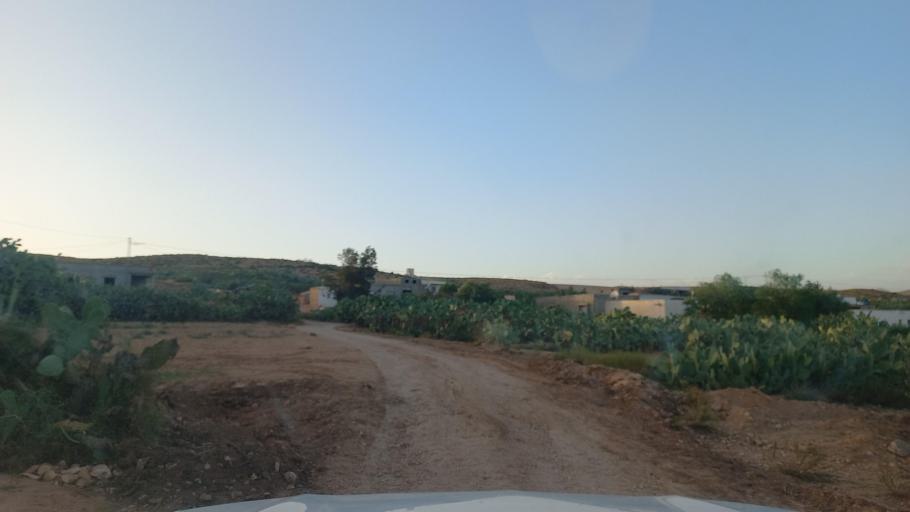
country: TN
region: Al Qasrayn
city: Sbiba
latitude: 35.3746
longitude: 9.0090
